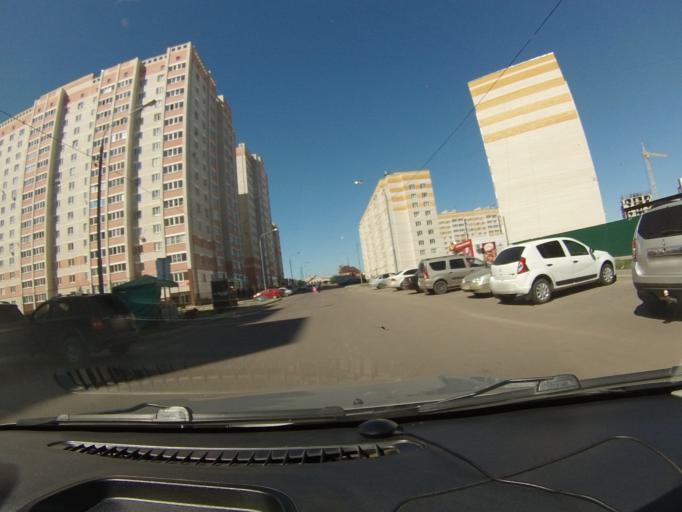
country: RU
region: Tambov
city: Tambov
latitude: 52.7751
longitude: 41.4020
